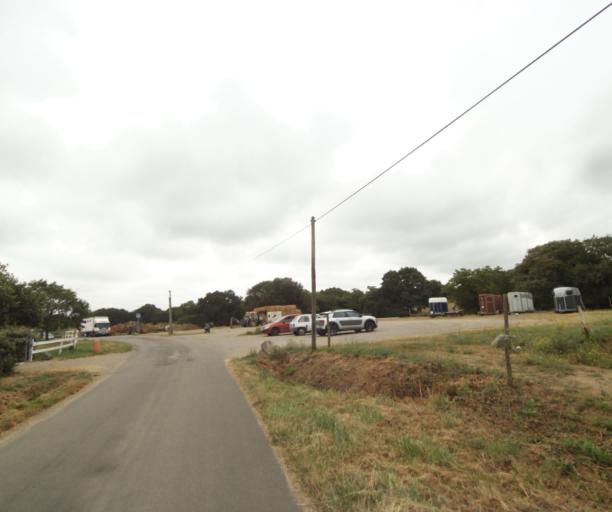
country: FR
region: Pays de la Loire
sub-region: Departement de la Vendee
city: Chateau-d'Olonne
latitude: 46.4849
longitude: -1.6882
